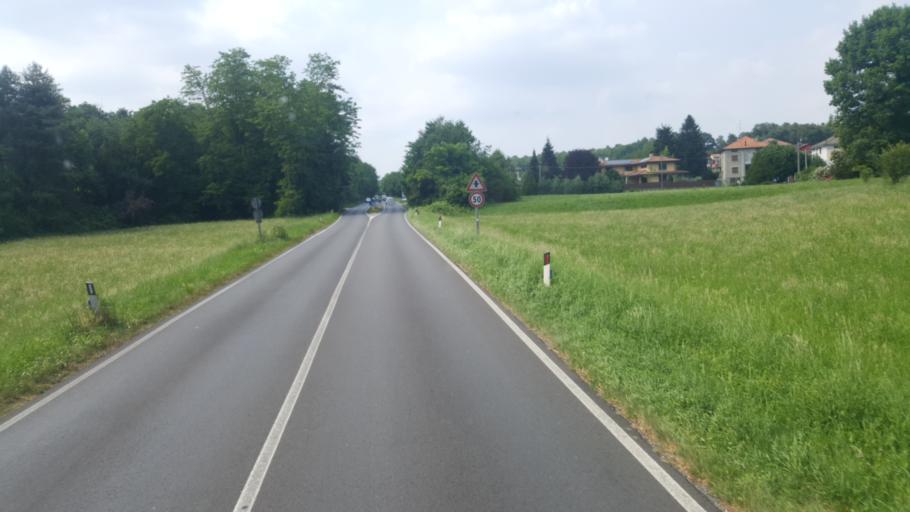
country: IT
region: Lombardy
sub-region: Provincia di Como
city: Oltrona di San Mamette
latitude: 45.7560
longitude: 8.9680
